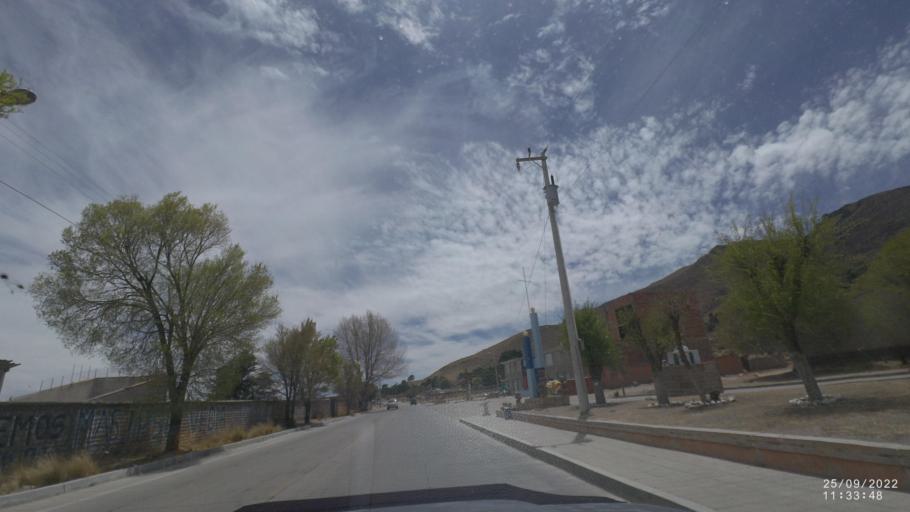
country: BO
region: Oruro
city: Challapata
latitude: -19.0084
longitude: -66.7761
